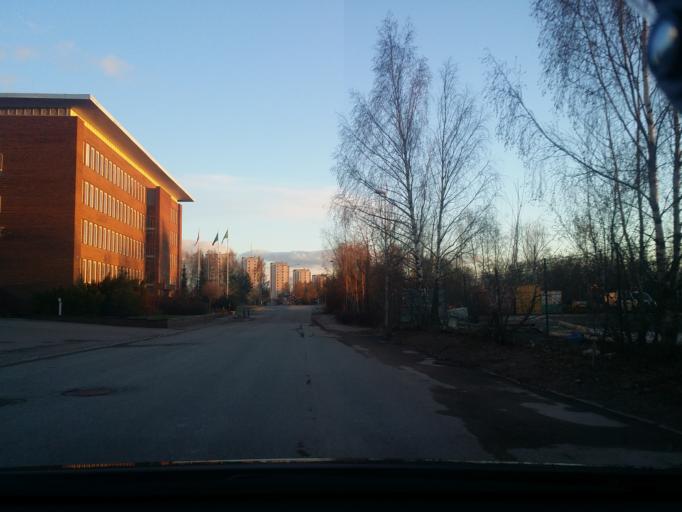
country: SE
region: Vaestmanland
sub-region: Vasteras
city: Vasteras
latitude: 59.6346
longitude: 16.5760
